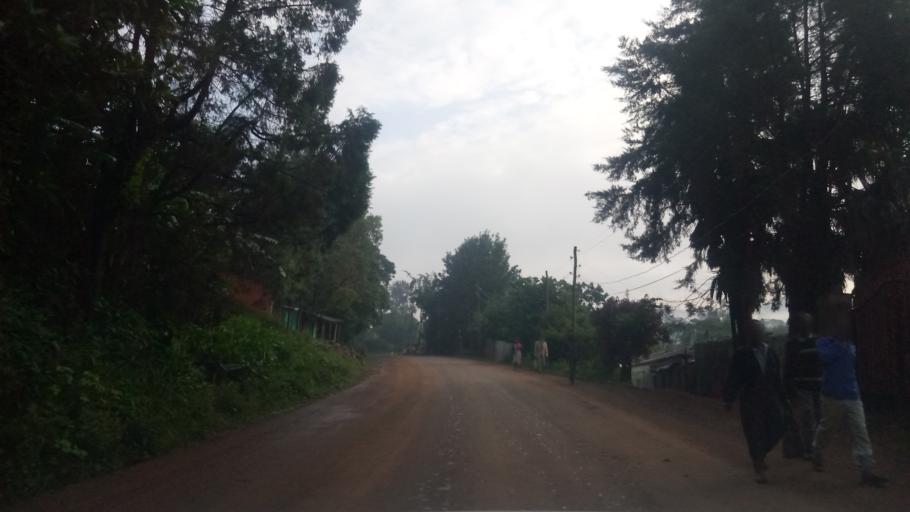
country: ET
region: Oromiya
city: Jima
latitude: 7.6811
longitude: 36.8341
